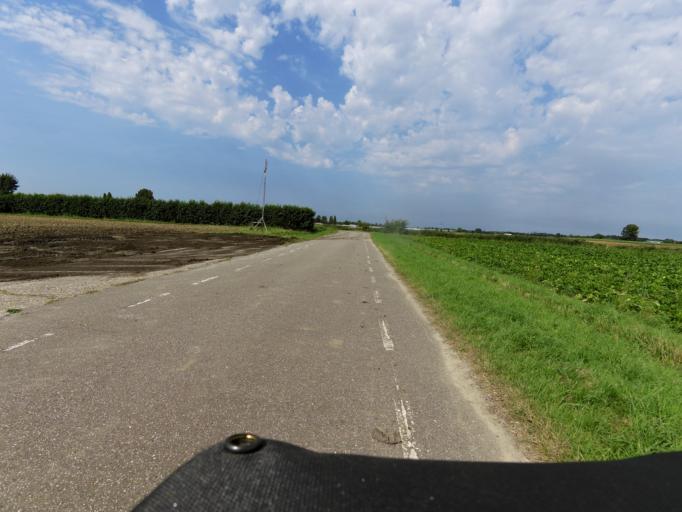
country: NL
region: South Holland
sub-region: Gemeente Binnenmaas
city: Heinenoord
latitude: 51.8131
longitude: 4.4454
